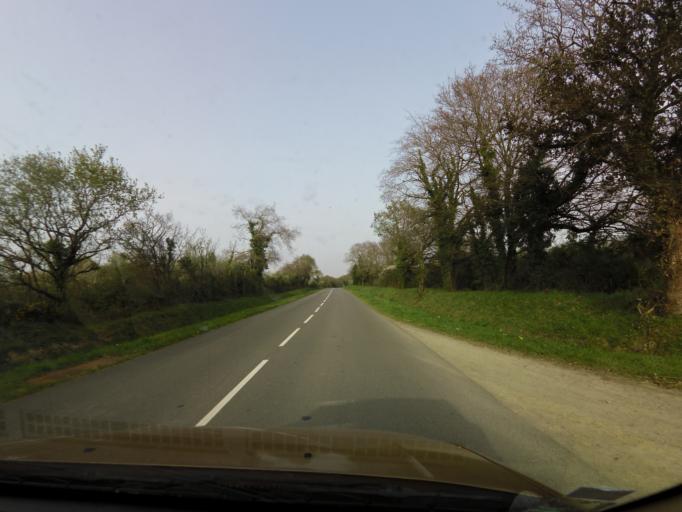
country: FR
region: Brittany
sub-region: Departement du Morbihan
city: Sene
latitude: 47.5763
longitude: -2.7031
